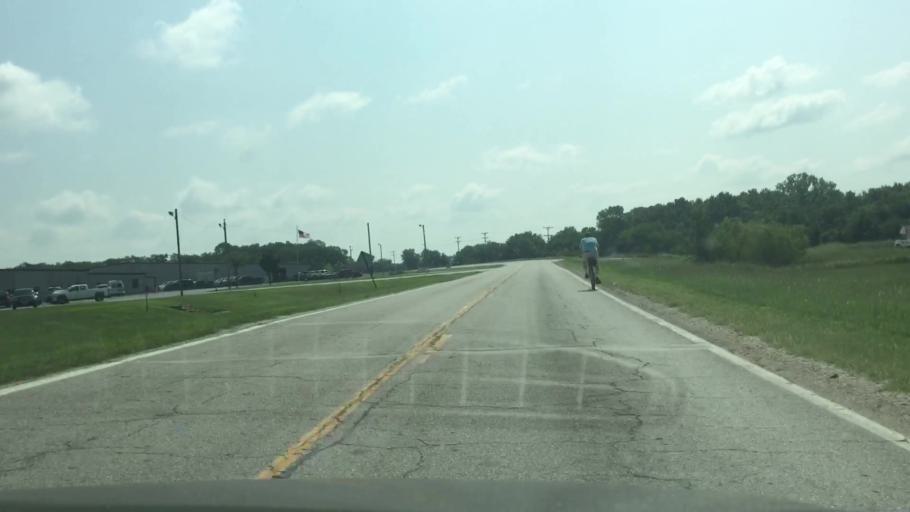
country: US
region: Kansas
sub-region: Allen County
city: Humboldt
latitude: 37.8215
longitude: -95.4329
